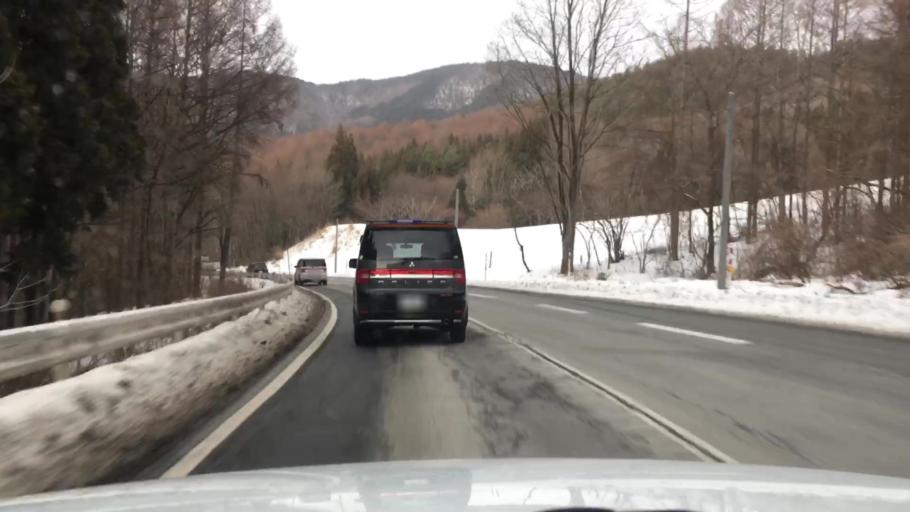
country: JP
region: Iwate
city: Morioka-shi
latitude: 39.6661
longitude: 141.3320
